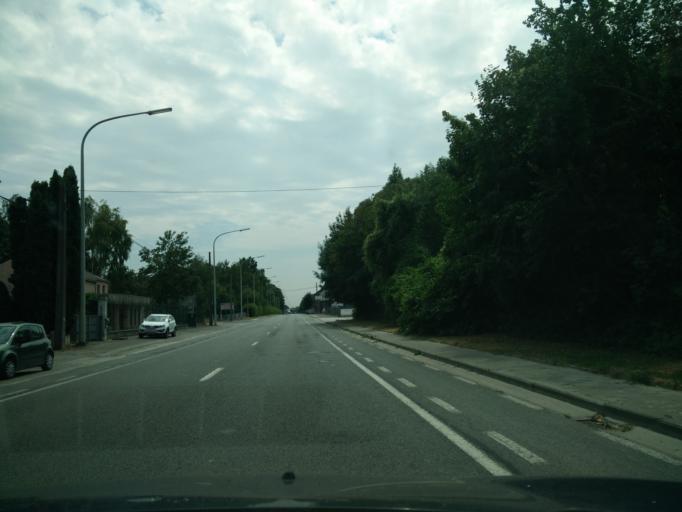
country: BE
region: Wallonia
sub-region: Province du Hainaut
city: Soignies
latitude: 50.5682
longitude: 4.0703
